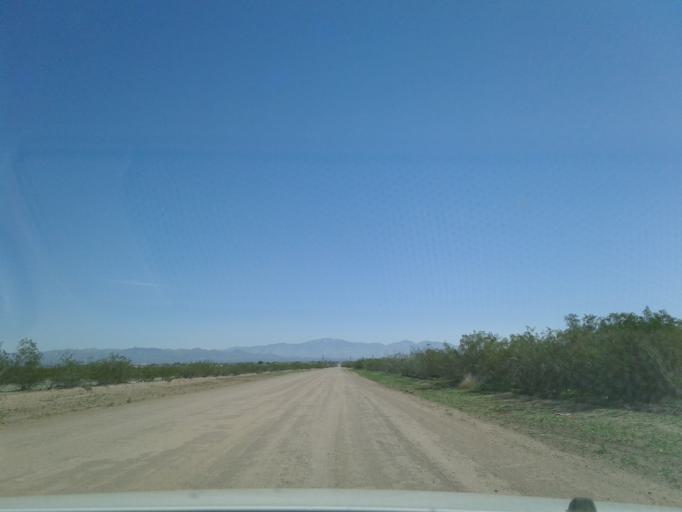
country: US
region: Arizona
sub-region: Pima County
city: Avra Valley
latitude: 32.4293
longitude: -111.3532
